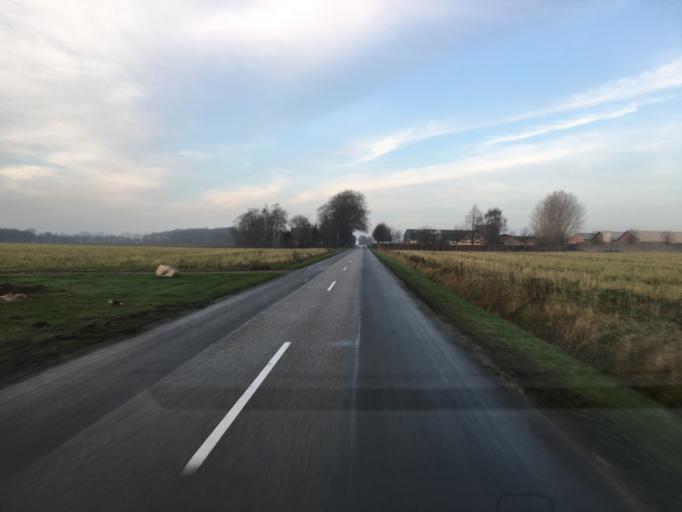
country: DK
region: South Denmark
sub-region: Tonder Kommune
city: Toftlund
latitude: 55.1292
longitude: 9.0624
